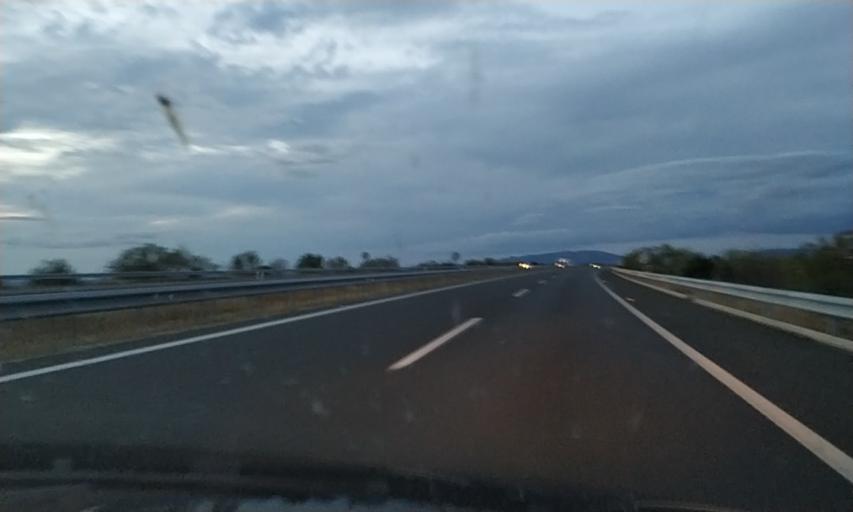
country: ES
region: Extremadura
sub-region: Provincia de Caceres
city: Santiago del Campo
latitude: 39.6446
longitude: -6.3949
